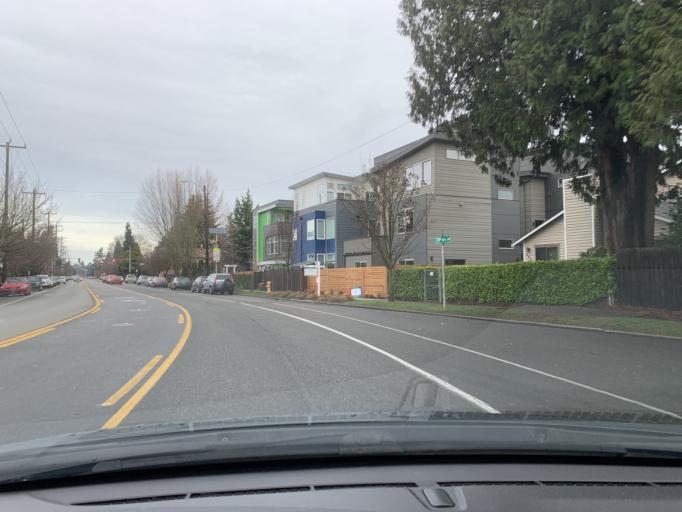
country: US
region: Washington
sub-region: King County
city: White Center
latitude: 47.5508
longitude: -122.3818
